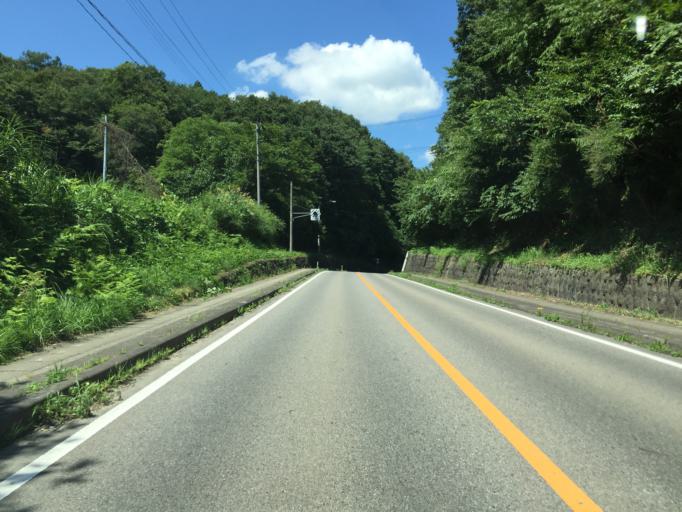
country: JP
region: Fukushima
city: Nihommatsu
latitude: 37.6422
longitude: 140.4629
